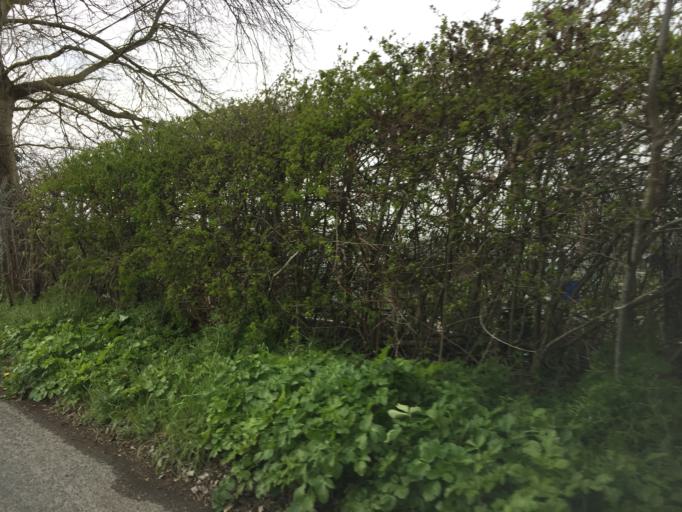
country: GB
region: England
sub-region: South Gloucestershire
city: Almondsbury
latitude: 51.5150
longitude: -2.5962
